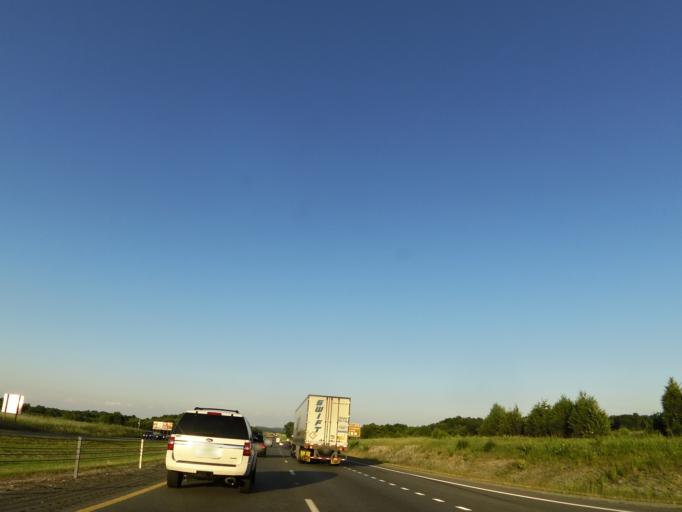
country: US
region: Tennessee
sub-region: Wilson County
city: Lebanon
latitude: 36.1827
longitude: -86.3193
